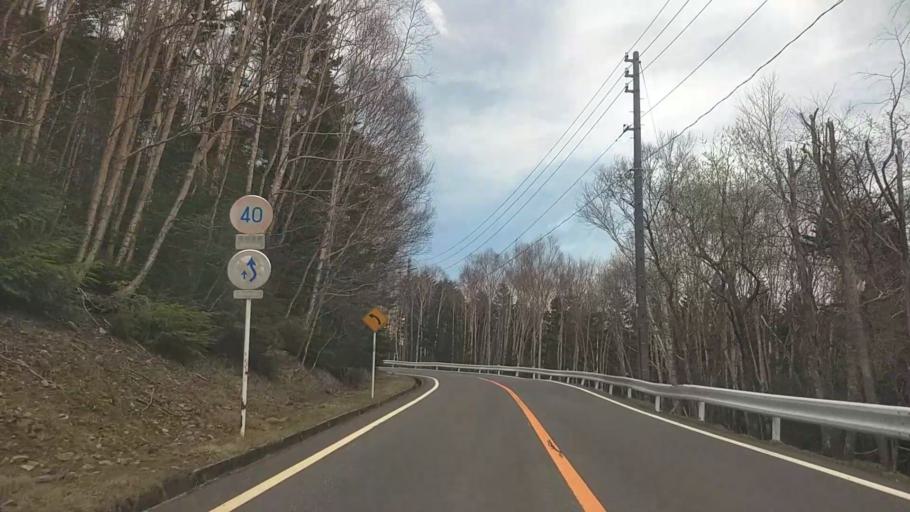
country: JP
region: Nagano
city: Saku
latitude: 36.0590
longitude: 138.3639
